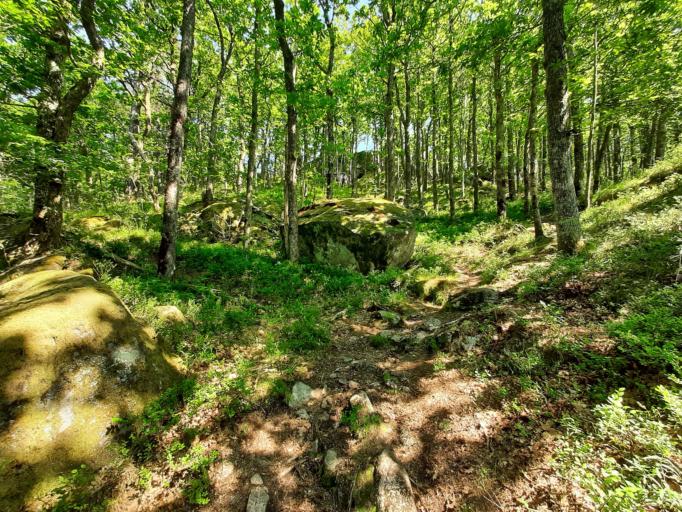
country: NO
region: Vest-Agder
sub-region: Songdalen
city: Nodeland
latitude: 58.1555
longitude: 7.8444
